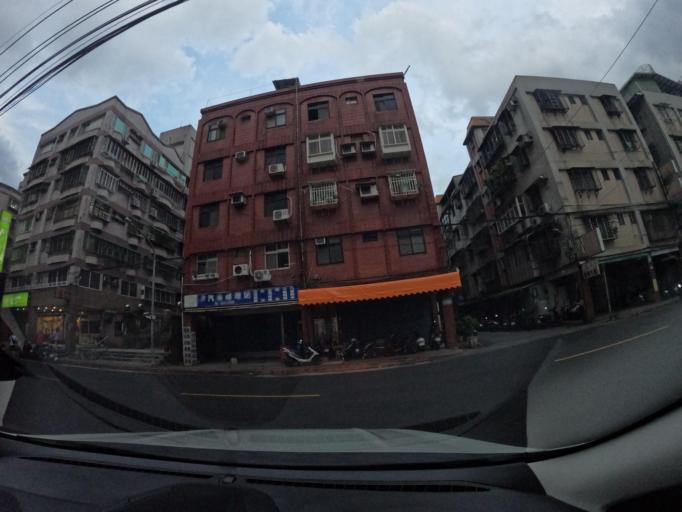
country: TW
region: Taipei
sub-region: Taipei
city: Banqiao
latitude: 24.9794
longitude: 121.4589
